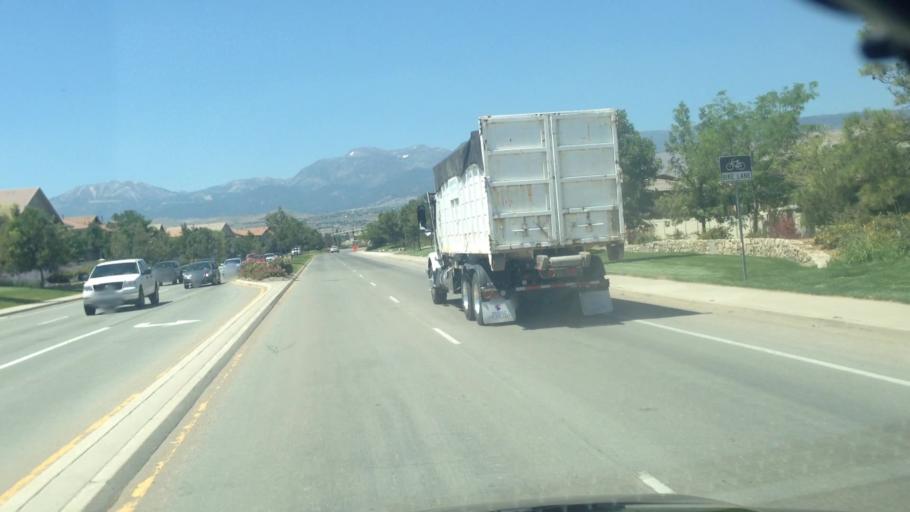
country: US
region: Nevada
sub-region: Washoe County
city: Sparks
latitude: 39.4246
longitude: -119.7295
